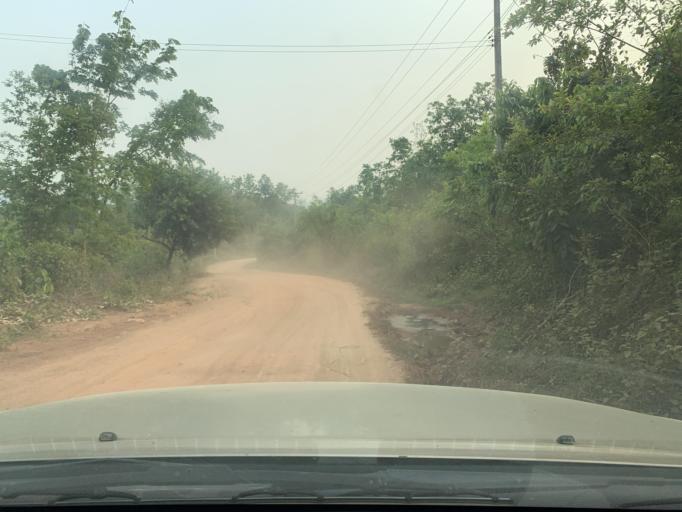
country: LA
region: Louangphabang
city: Louangphabang
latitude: 19.9204
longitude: 102.0757
